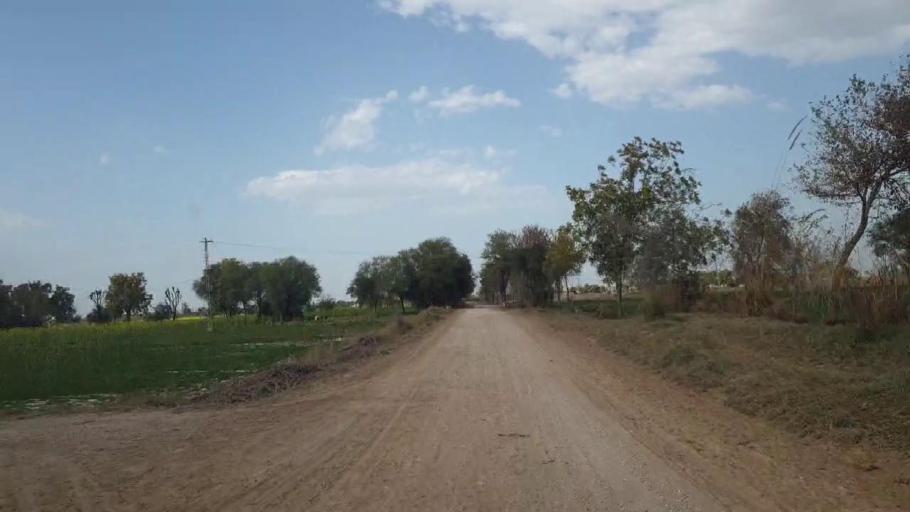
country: PK
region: Sindh
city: Shahdadpur
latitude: 26.0039
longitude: 68.4591
